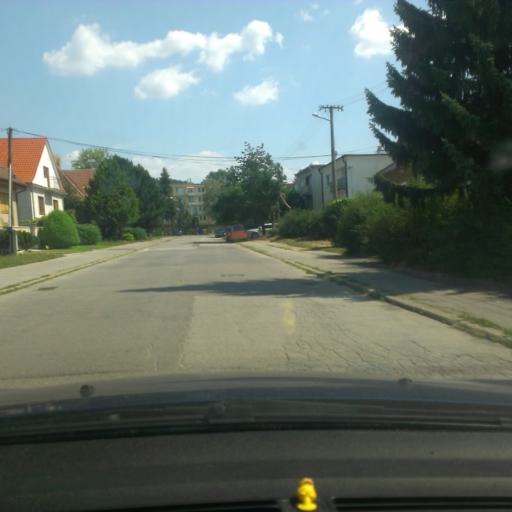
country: SK
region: Trnavsky
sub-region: Okres Trnava
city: Piestany
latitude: 48.5839
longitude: 17.8302
